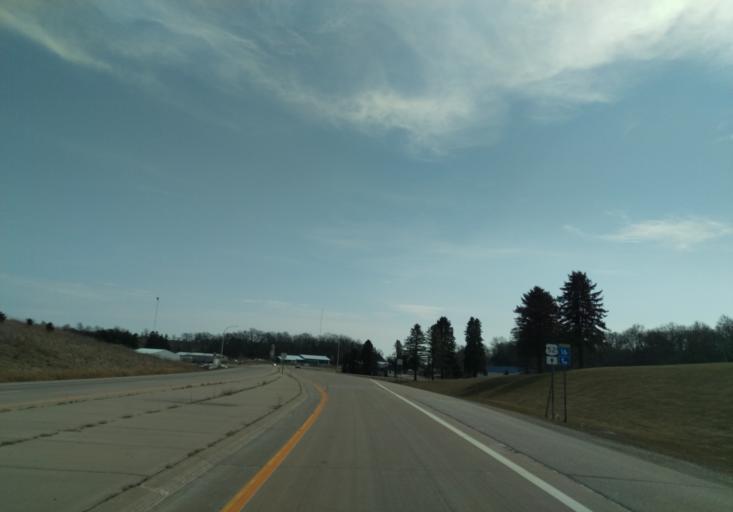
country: US
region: Minnesota
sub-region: Fillmore County
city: Preston
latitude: 43.6868
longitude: -92.0956
